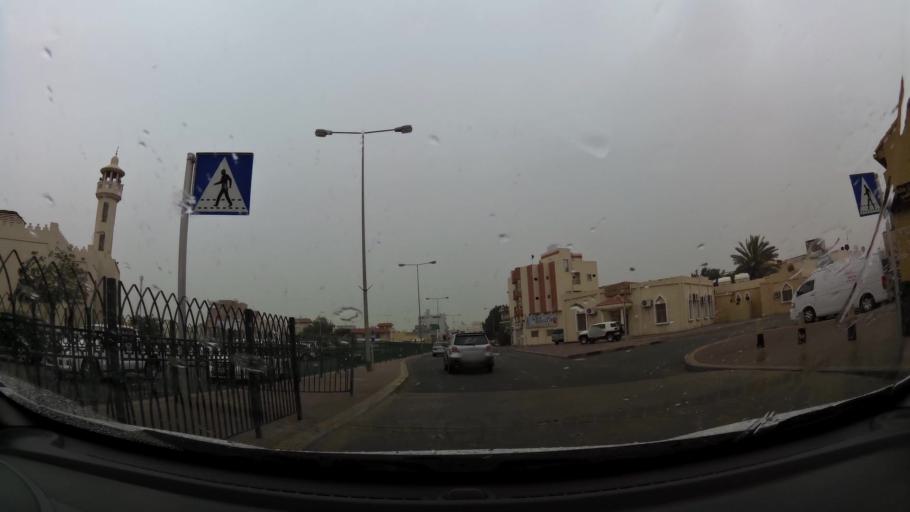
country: BH
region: Northern
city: Madinat `Isa
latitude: 26.1694
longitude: 50.5570
